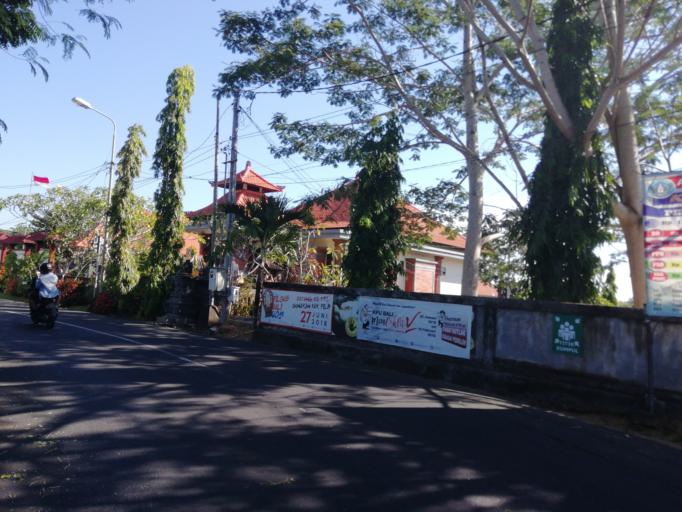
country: ID
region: Bali
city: Jimbaran
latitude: -8.8295
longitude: 115.1773
